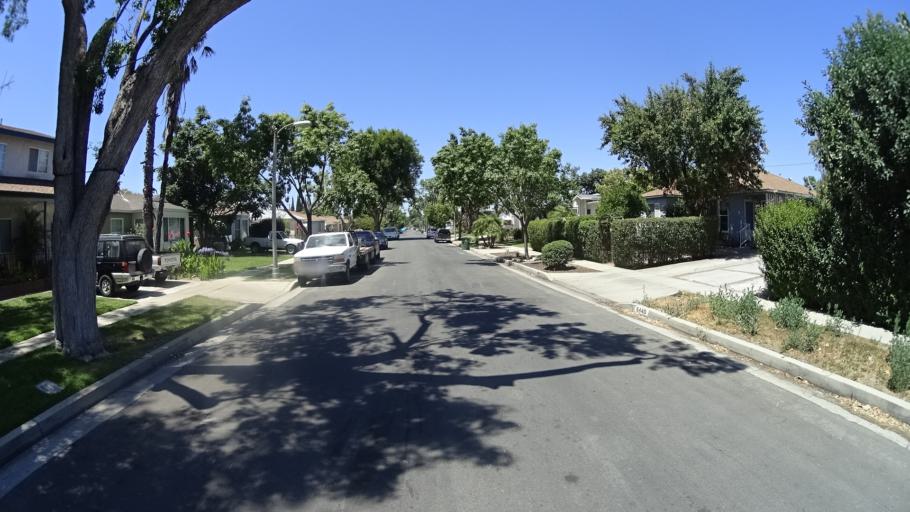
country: US
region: California
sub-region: Los Angeles County
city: Northridge
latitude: 34.1880
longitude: -118.5215
